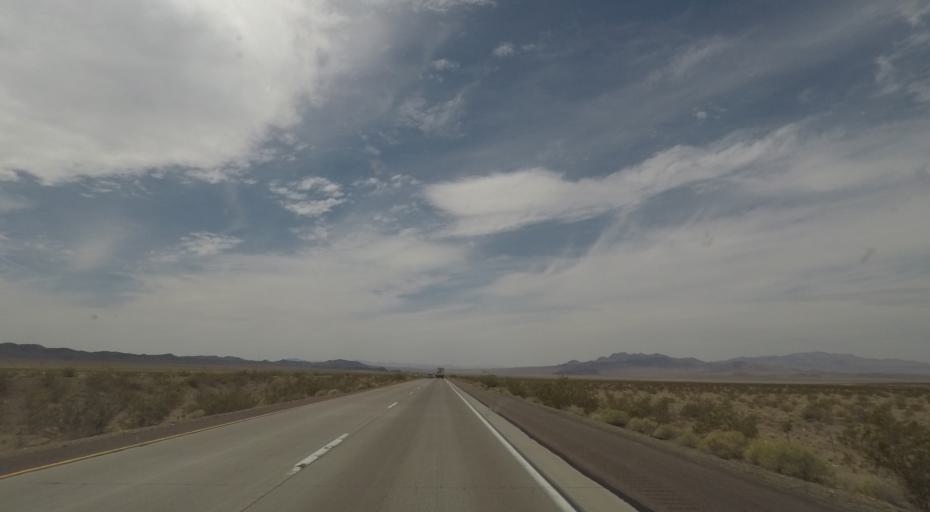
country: US
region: California
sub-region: San Bernardino County
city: Twentynine Palms
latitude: 34.7276
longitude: -116.0928
